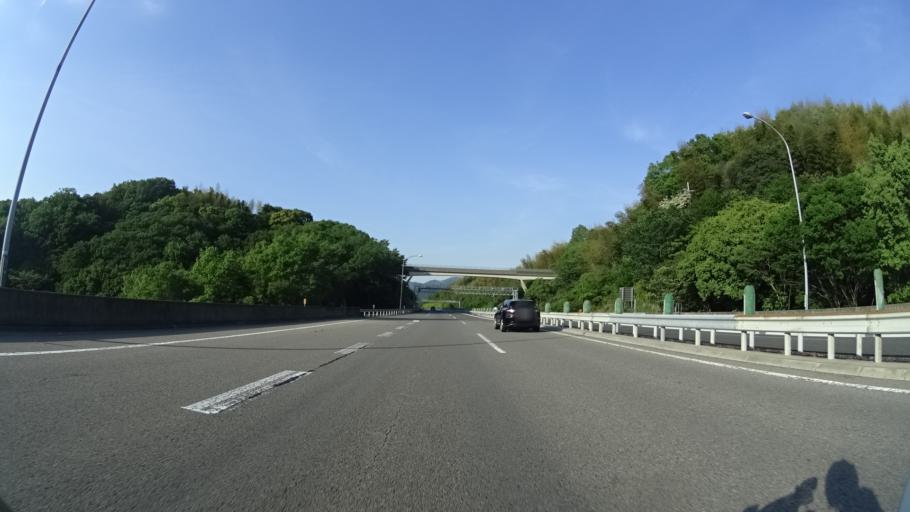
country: JP
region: Ehime
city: Kawanoecho
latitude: 33.9852
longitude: 133.5886
